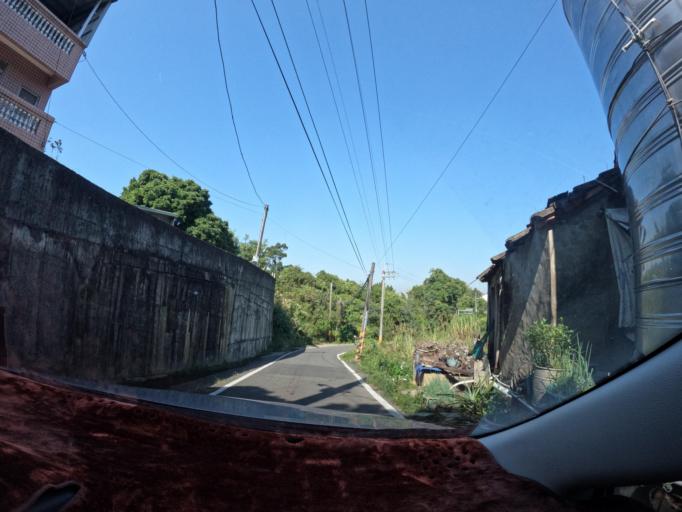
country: TW
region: Taiwan
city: Yujing
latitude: 23.0443
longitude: 120.3646
